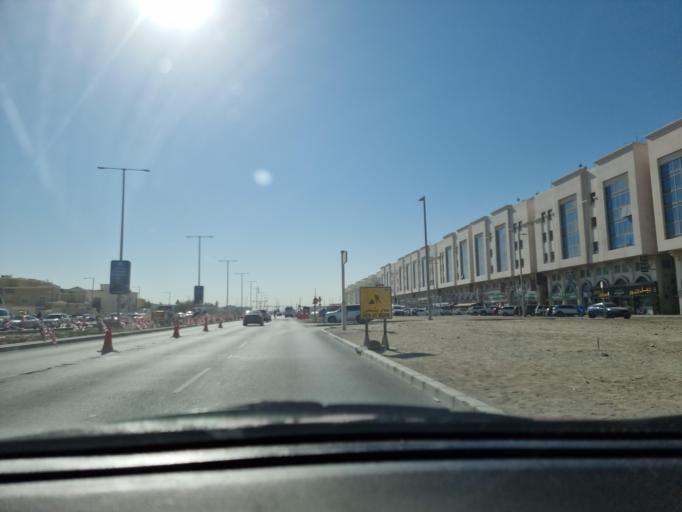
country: AE
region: Abu Dhabi
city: Abu Dhabi
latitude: 24.4229
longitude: 54.5655
